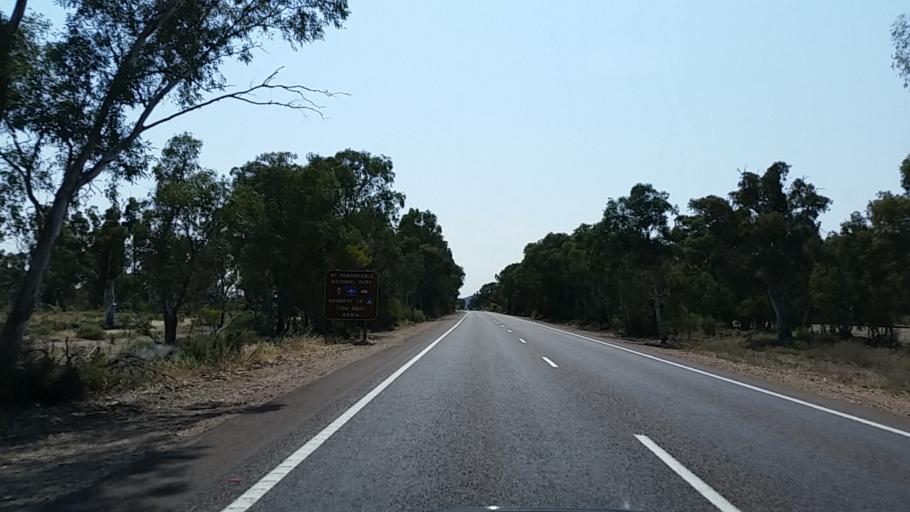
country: AU
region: South Australia
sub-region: Port Pirie City and Dists
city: Port Pirie
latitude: -32.8551
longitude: 137.9821
